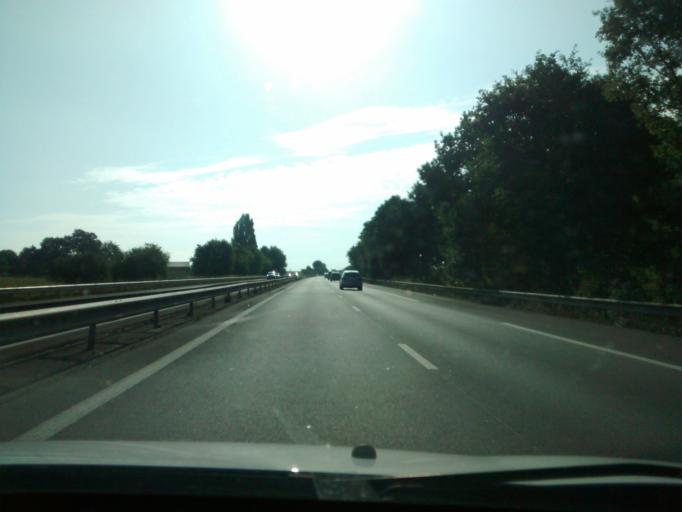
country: FR
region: Brittany
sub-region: Departement d'Ille-et-Vilaine
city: Saint-Didier
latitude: 48.0881
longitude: -1.3600
